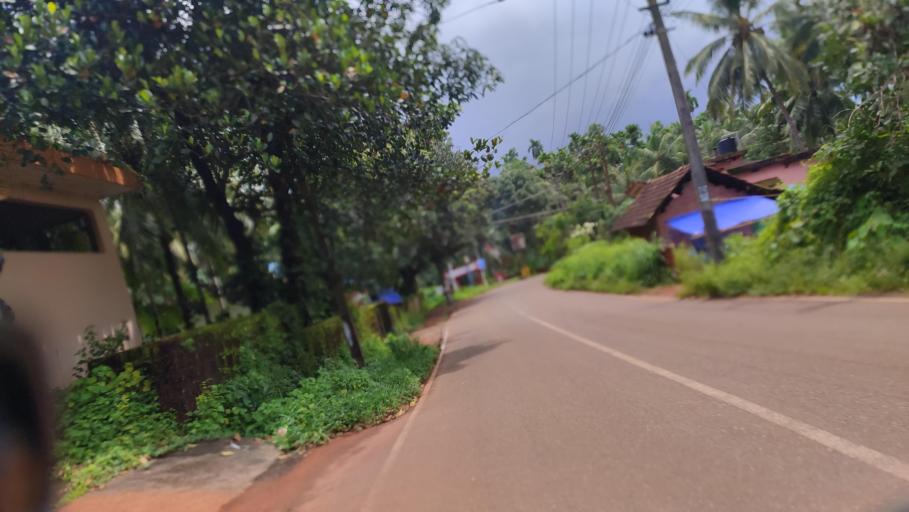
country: IN
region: Kerala
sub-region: Kasaragod District
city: Kannangad
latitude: 12.3953
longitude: 75.0538
